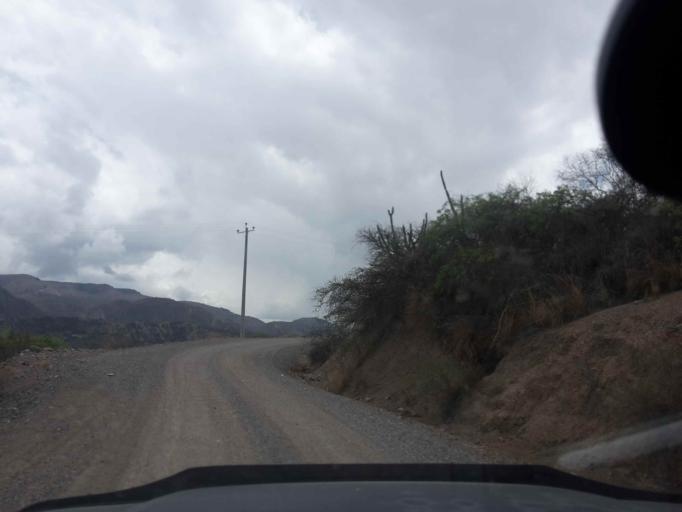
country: BO
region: Cochabamba
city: Sipe Sipe
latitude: -17.5434
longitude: -66.4808
